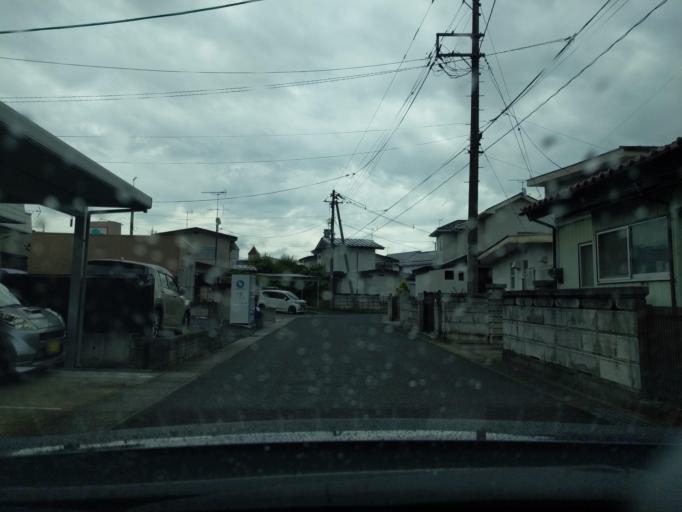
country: JP
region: Fukushima
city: Koriyama
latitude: 37.3677
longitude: 140.3583
